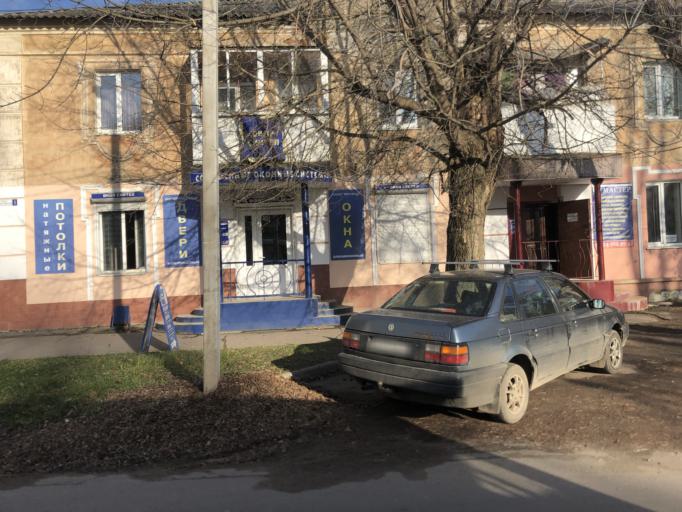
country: RU
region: Tverskaya
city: Rzhev
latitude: 56.2625
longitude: 34.3385
